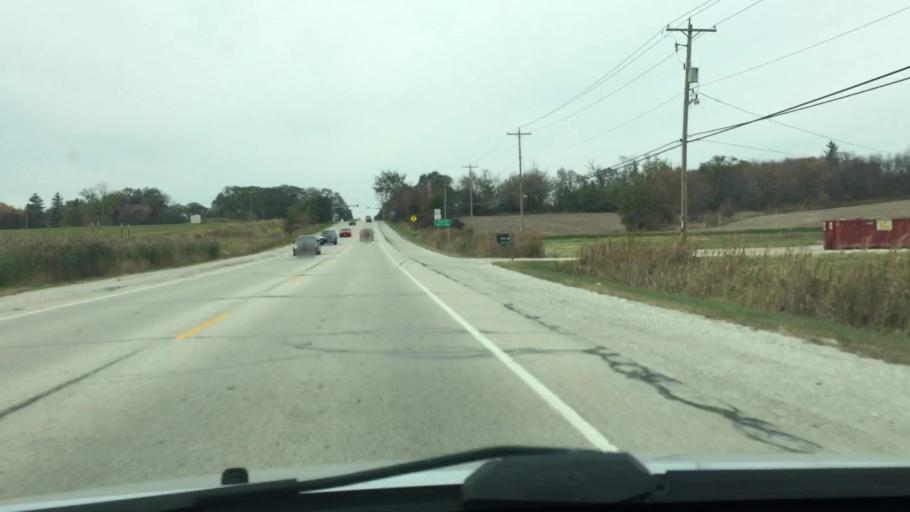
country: US
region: Wisconsin
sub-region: Milwaukee County
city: Franklin
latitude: 42.8726
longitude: -88.0054
